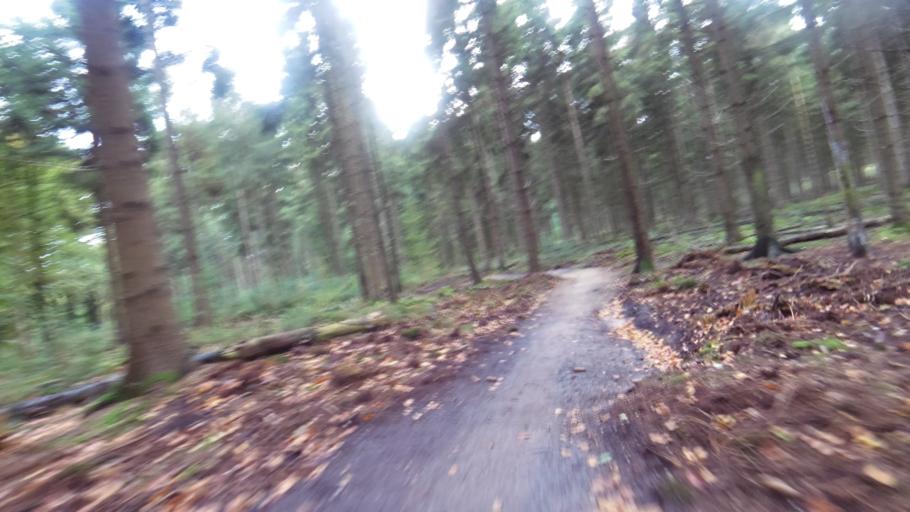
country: NL
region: Gelderland
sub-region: Gemeente Ede
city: Wekerom
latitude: 52.0791
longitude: 5.7340
